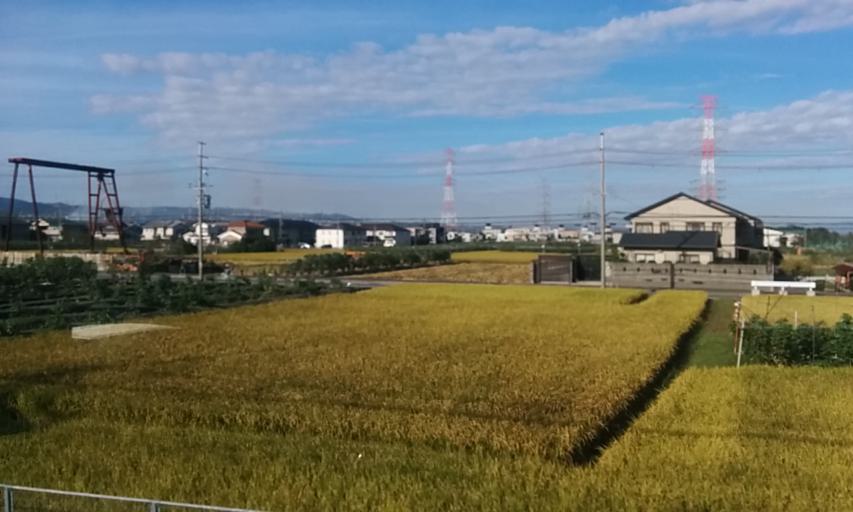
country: JP
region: Kyoto
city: Tanabe
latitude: 34.8424
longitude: 135.7726
